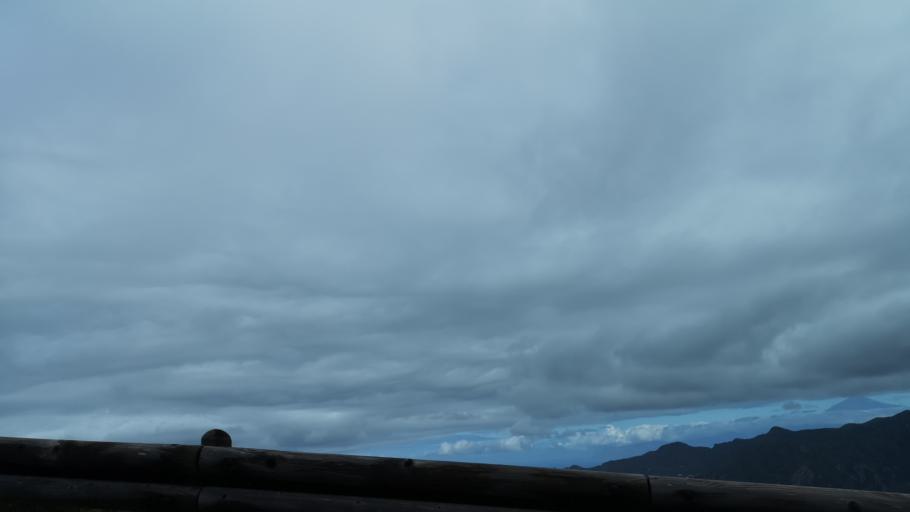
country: ES
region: Canary Islands
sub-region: Provincia de Santa Cruz de Tenerife
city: Vallehermosa
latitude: 28.1633
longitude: -17.2929
